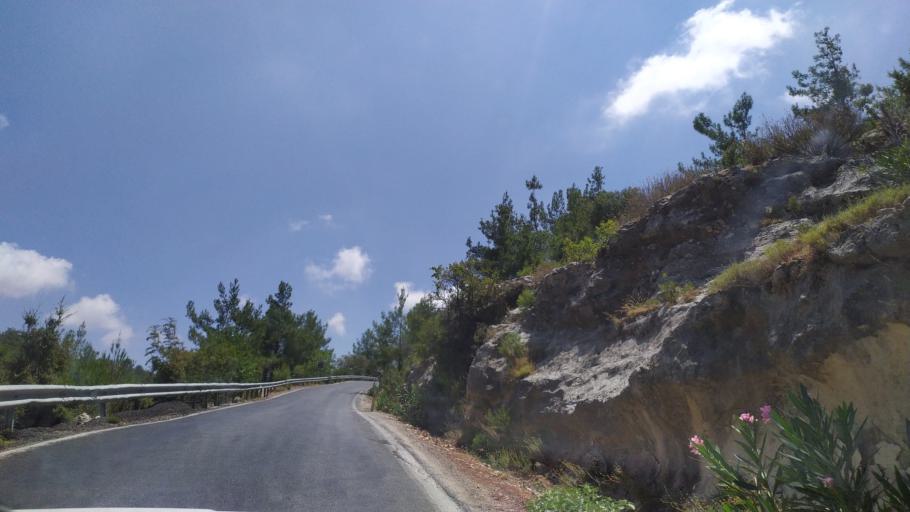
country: TR
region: Mersin
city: Gulnar
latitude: 36.2774
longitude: 33.3797
